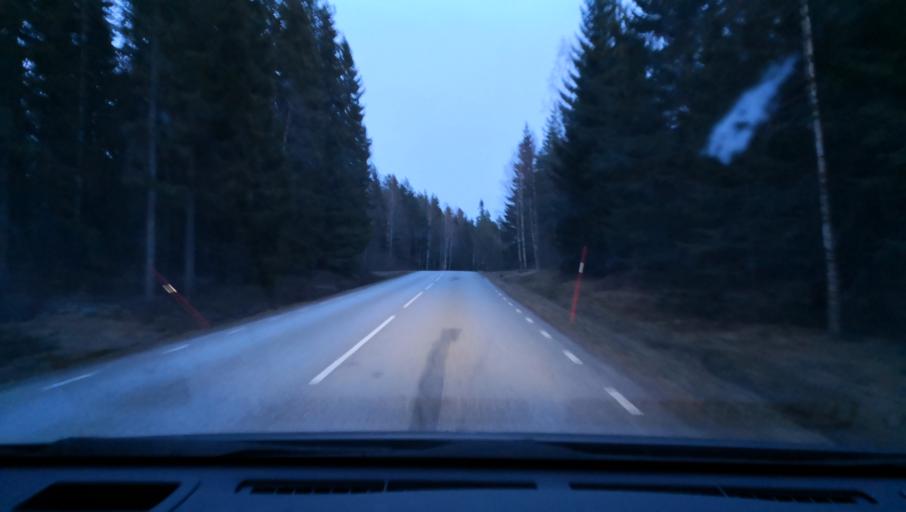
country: SE
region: OErebro
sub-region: Lindesbergs Kommun
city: Frovi
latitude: 59.5977
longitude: 15.3707
